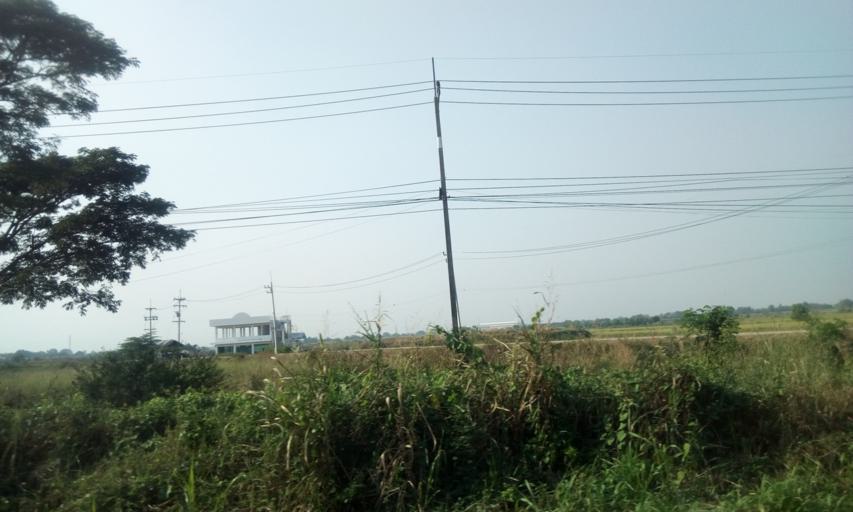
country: TH
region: Sing Buri
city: Phrom Buri
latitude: 14.7609
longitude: 100.4379
